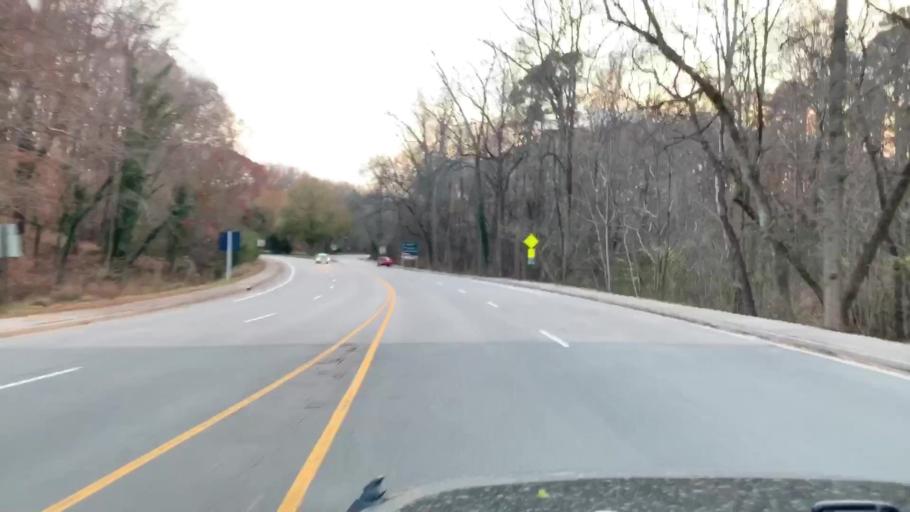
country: US
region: Virginia
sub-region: City of Williamsburg
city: Williamsburg
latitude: 37.2828
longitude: -76.7017
